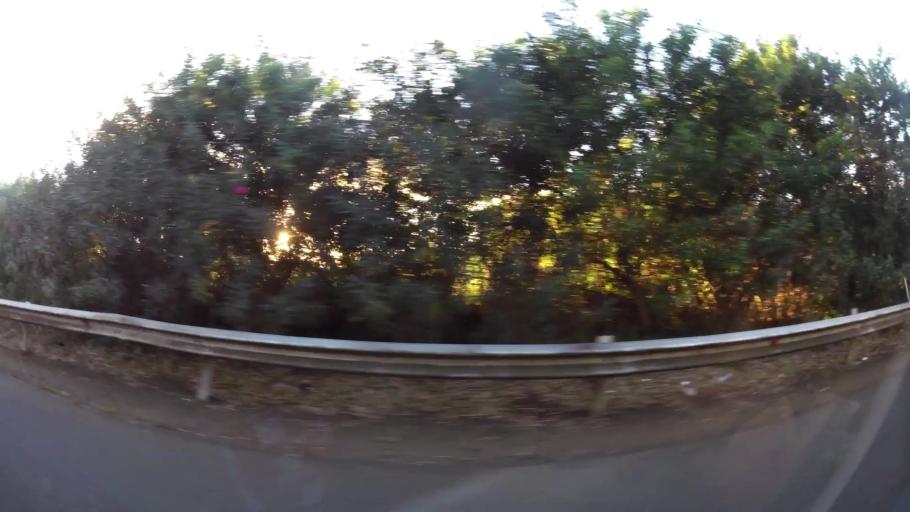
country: MU
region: Plaines Wilhems
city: Ebene
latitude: -20.2413
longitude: 57.4943
